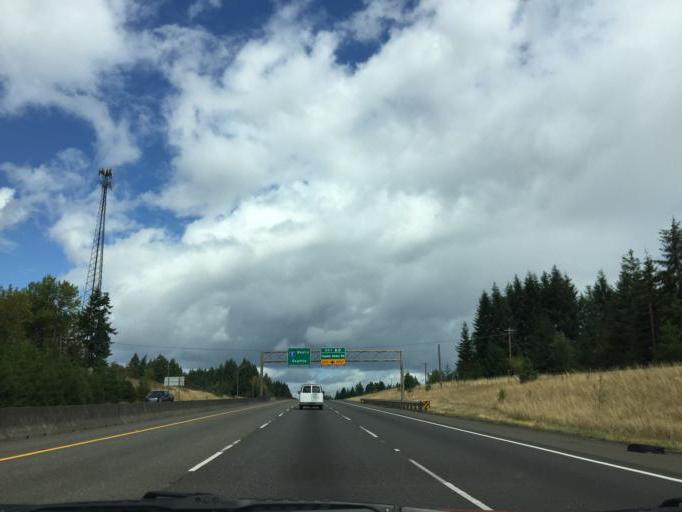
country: US
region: Washington
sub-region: Lewis County
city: Winlock
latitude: 46.4315
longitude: -122.8896
